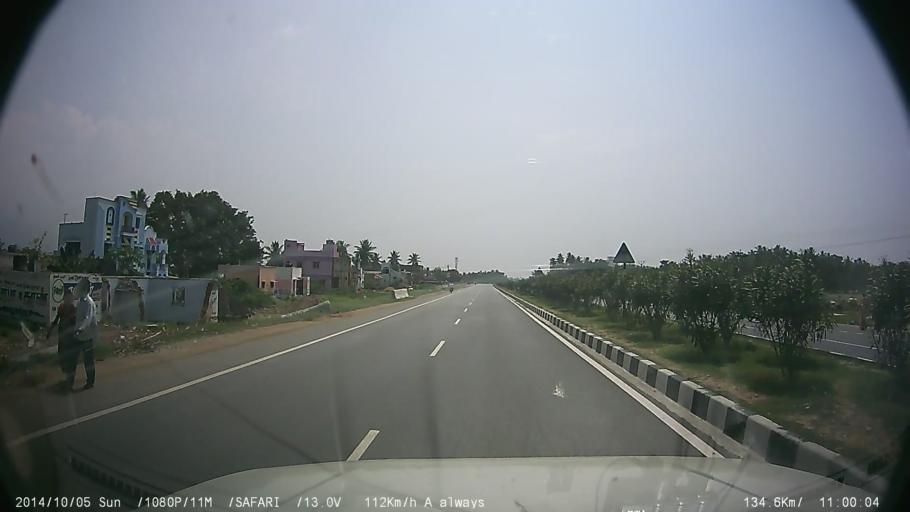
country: IN
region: Tamil Nadu
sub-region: Salem
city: Attur
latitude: 11.6269
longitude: 78.5395
